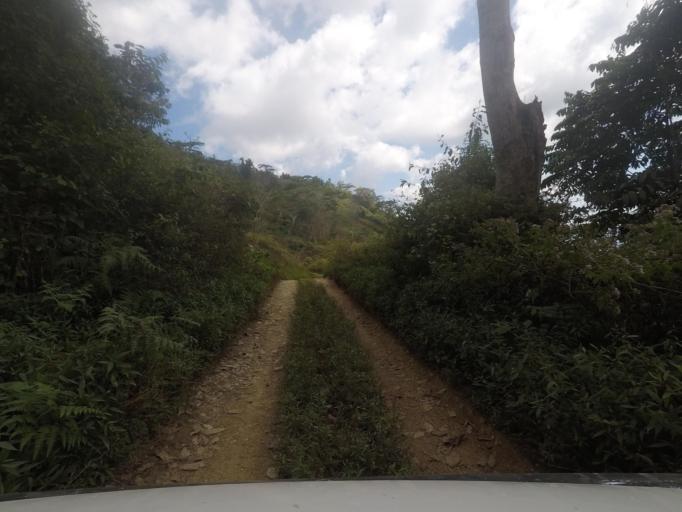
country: TL
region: Ermera
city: Gleno
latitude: -8.7497
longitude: 125.3213
